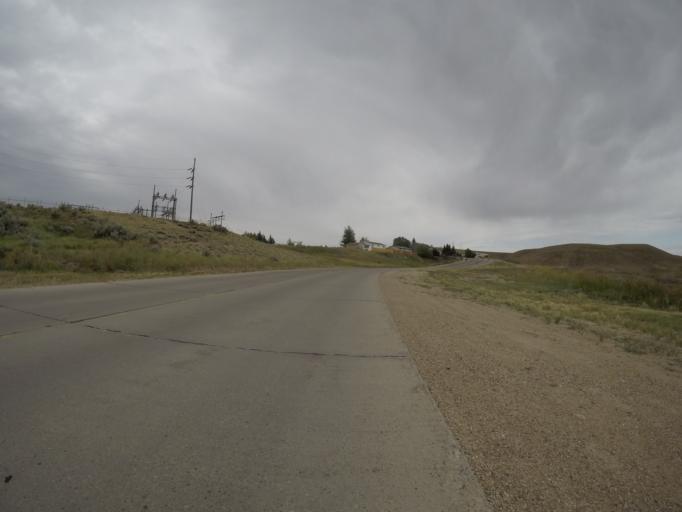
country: US
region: Wyoming
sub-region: Lincoln County
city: Kemmerer
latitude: 41.7918
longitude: -110.5483
